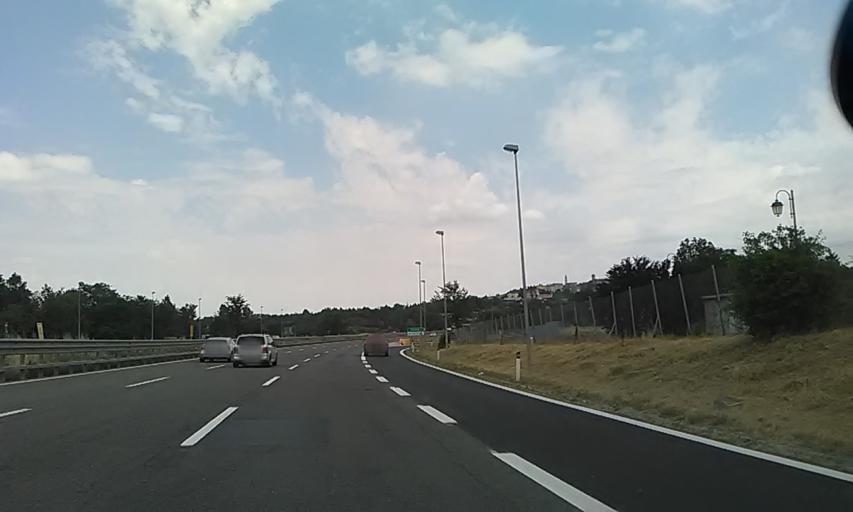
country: IT
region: Piedmont
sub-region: Provincia di Alessandria
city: Belforte Monferrato
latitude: 44.6264
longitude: 8.6581
